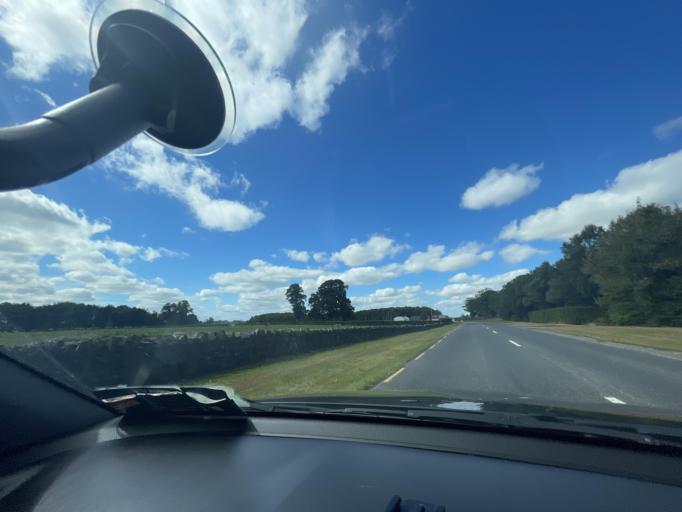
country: IE
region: Leinster
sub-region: An Mhi
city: Dunshaughlin
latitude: 53.5230
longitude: -6.6566
